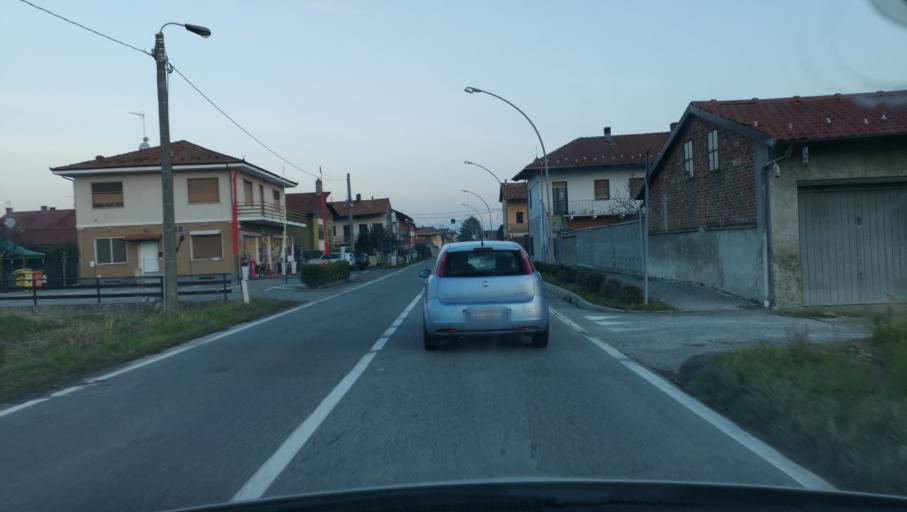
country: IT
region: Piedmont
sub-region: Provincia di Torino
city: Caluso
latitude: 45.2824
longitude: 7.8927
